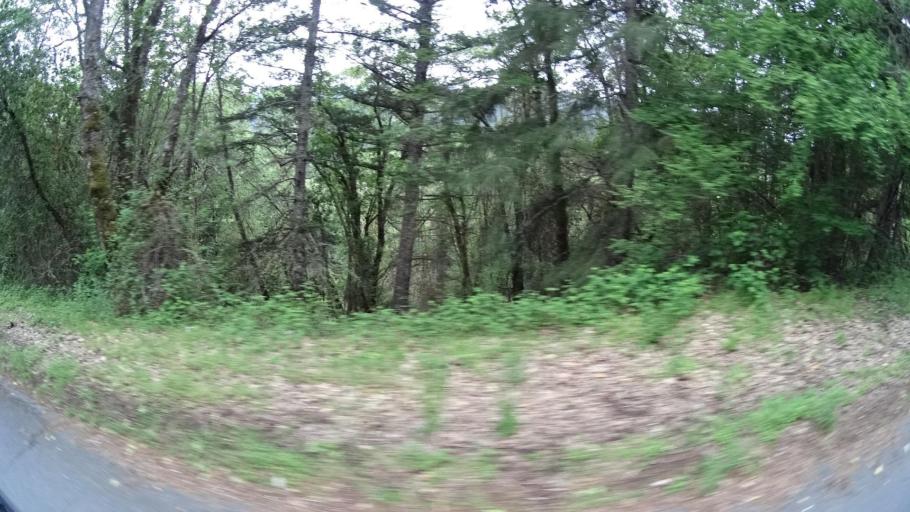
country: US
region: California
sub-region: Humboldt County
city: Willow Creek
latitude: 41.1056
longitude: -123.7124
